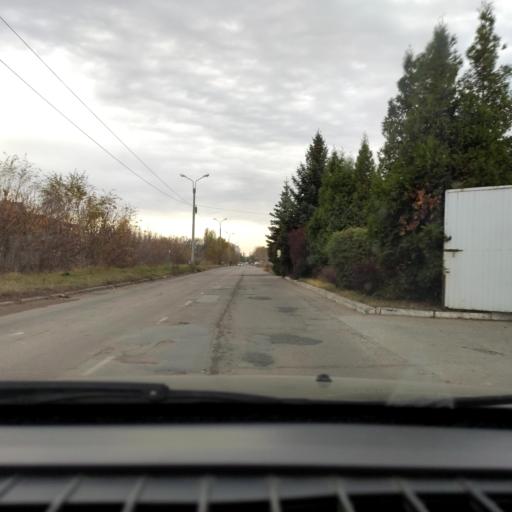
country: RU
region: Samara
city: Tol'yatti
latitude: 53.5575
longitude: 49.3146
